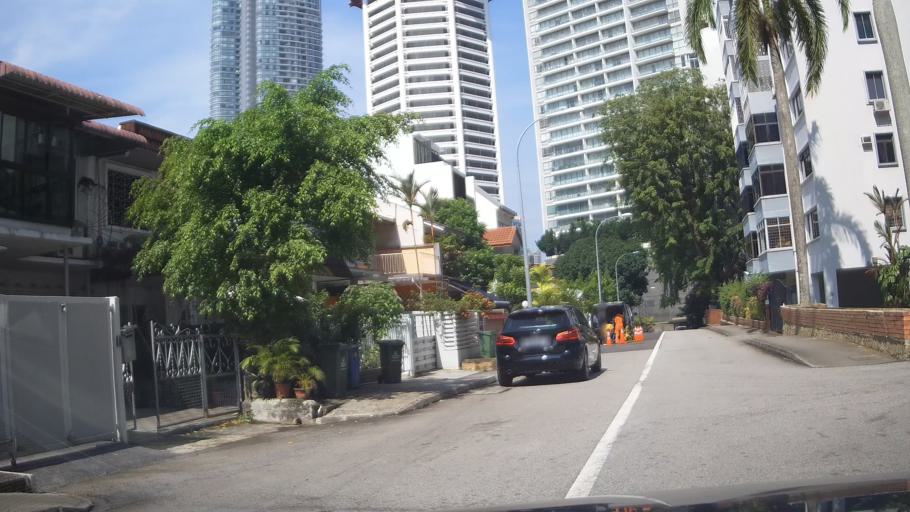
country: SG
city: Singapore
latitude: 1.3058
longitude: 103.8349
